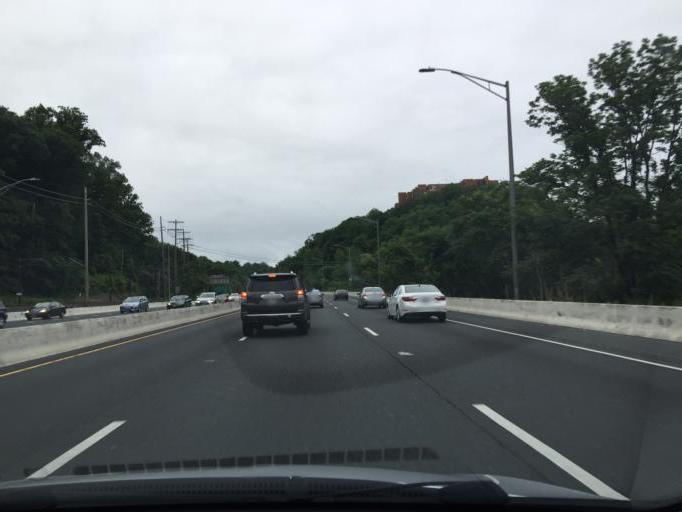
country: US
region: Maryland
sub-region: Baltimore County
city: Towson
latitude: 39.3526
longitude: -76.6471
